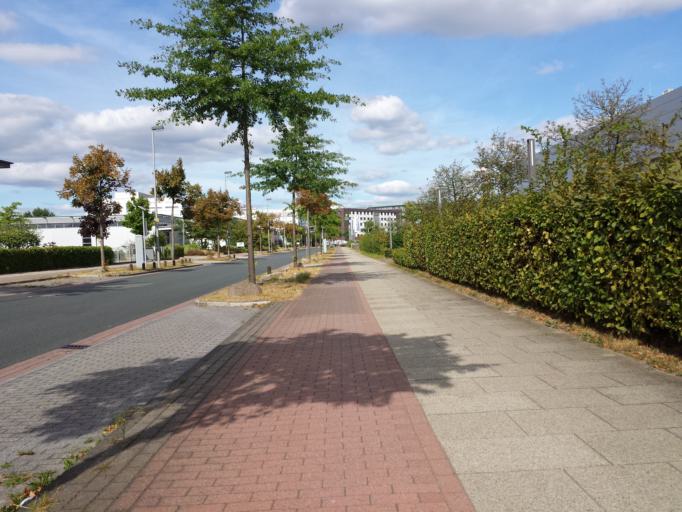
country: DE
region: Lower Saxony
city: Stuhr
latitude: 53.0532
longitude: 8.7765
